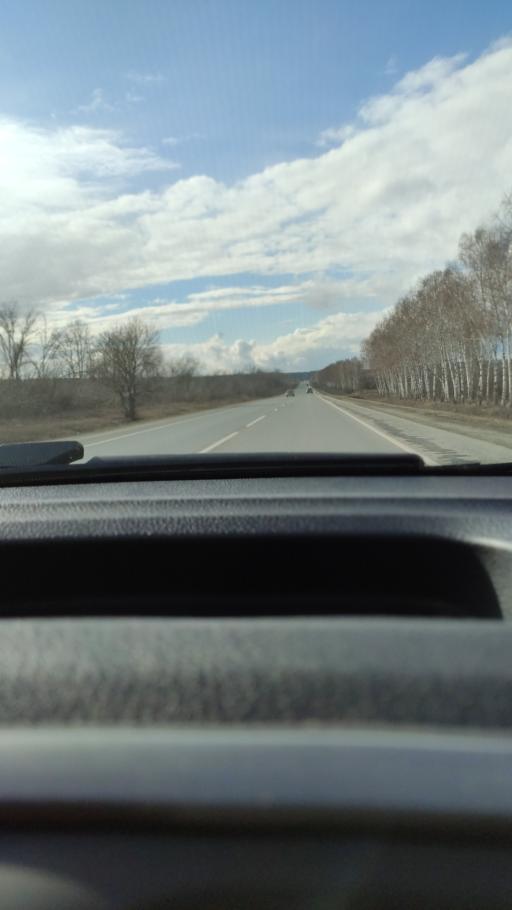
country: RU
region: Samara
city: Kurumoch
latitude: 53.4868
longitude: 50.0093
